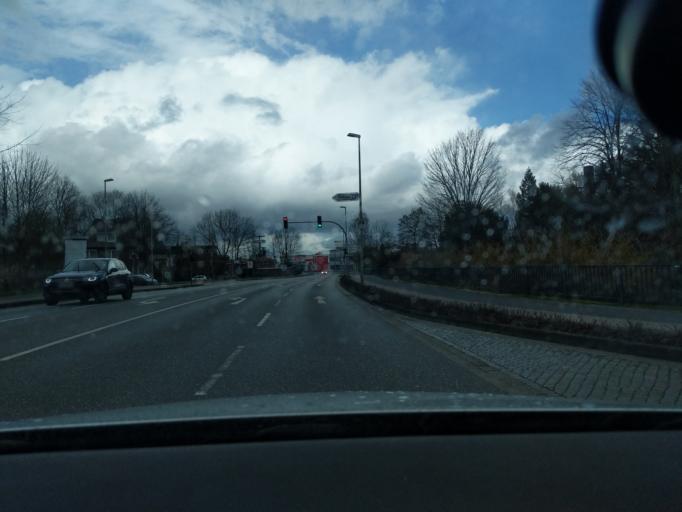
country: DE
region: Lower Saxony
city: Stade
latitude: 53.6050
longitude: 9.4778
